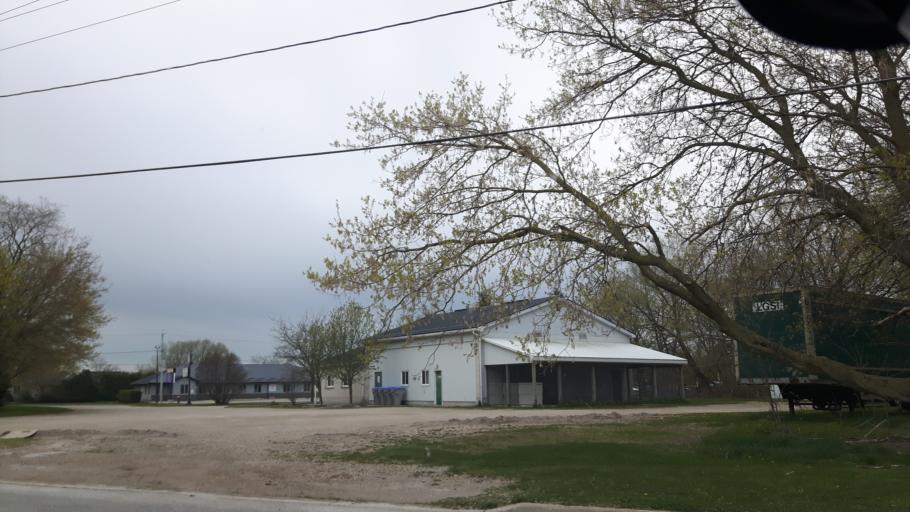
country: CA
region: Ontario
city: Bluewater
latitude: 43.6216
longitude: -81.5476
